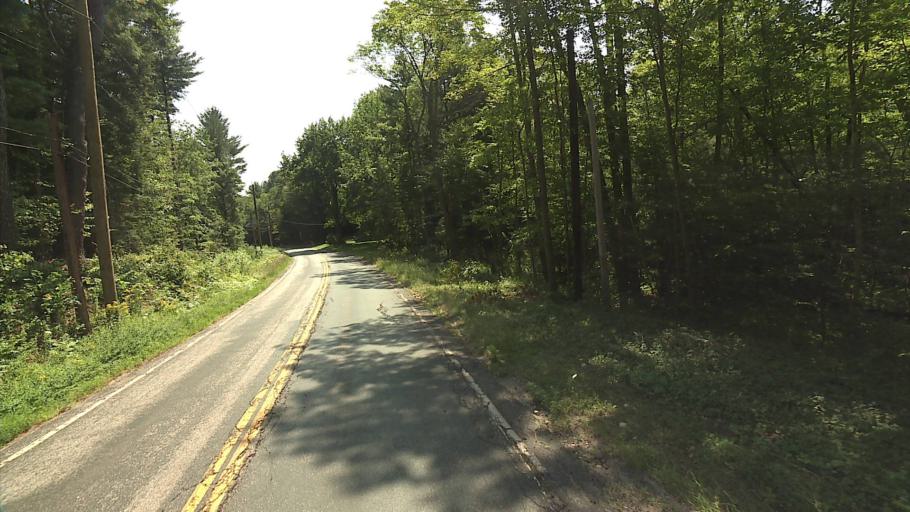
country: US
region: Connecticut
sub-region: Litchfield County
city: Winchester Center
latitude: 41.9201
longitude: -73.2030
